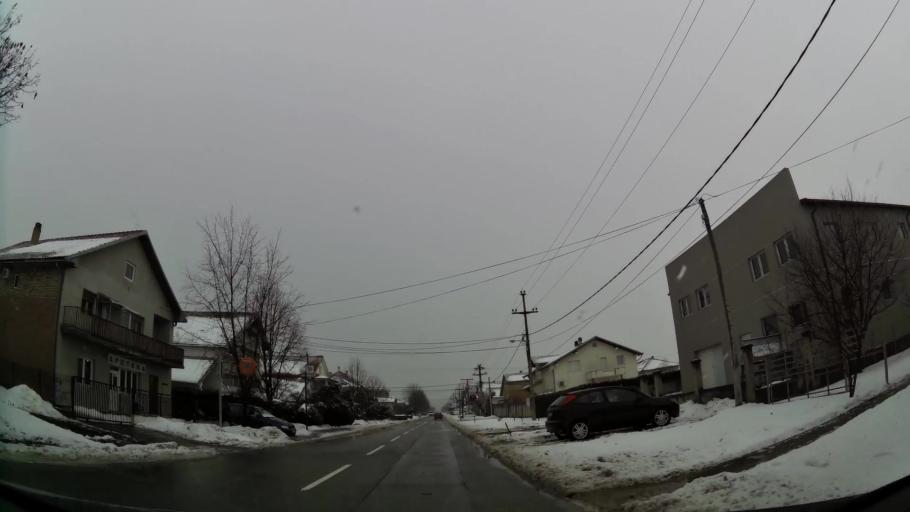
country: RS
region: Central Serbia
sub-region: Belgrade
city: Zemun
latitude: 44.8500
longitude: 20.3390
